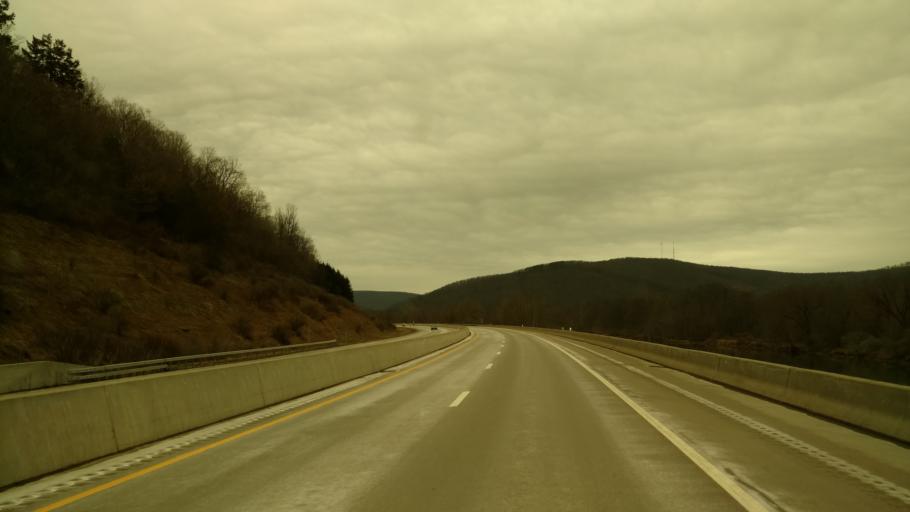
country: US
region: New York
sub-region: Cattaraugus County
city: Salamanca
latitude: 42.1405
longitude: -78.6659
